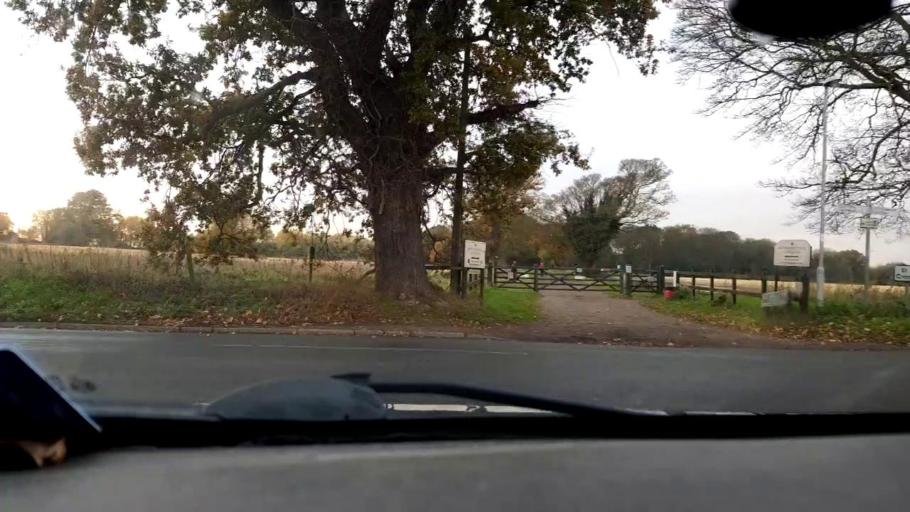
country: GB
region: England
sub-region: Norfolk
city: Spixworth
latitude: 52.6879
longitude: 1.3170
